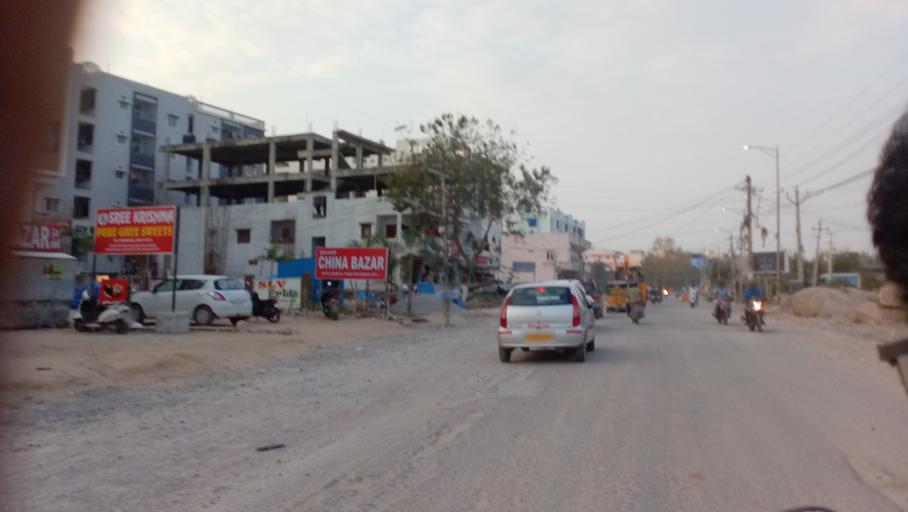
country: IN
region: Telangana
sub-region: Medak
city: Serilingampalle
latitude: 17.5096
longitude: 78.3183
